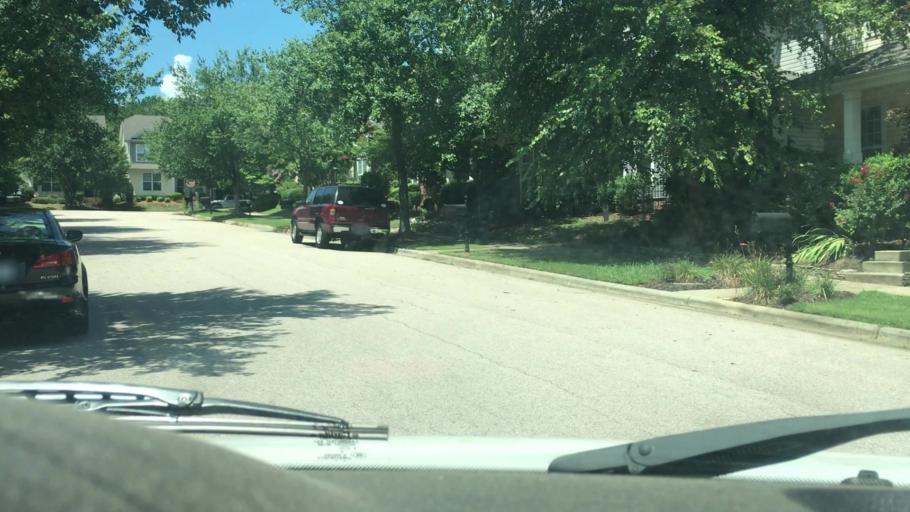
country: US
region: North Carolina
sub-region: Mecklenburg County
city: Cornelius
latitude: 35.4615
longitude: -80.8627
